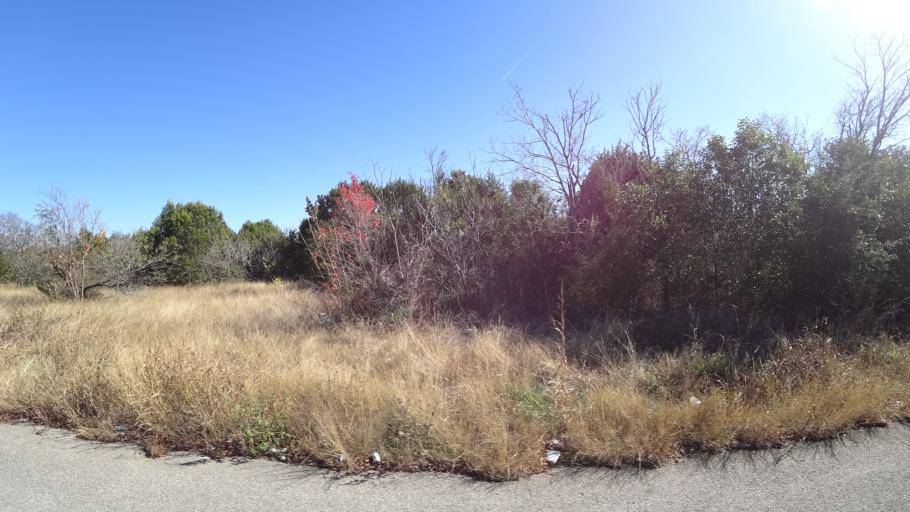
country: US
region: Texas
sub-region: Travis County
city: Wells Branch
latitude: 30.4243
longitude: -97.7013
